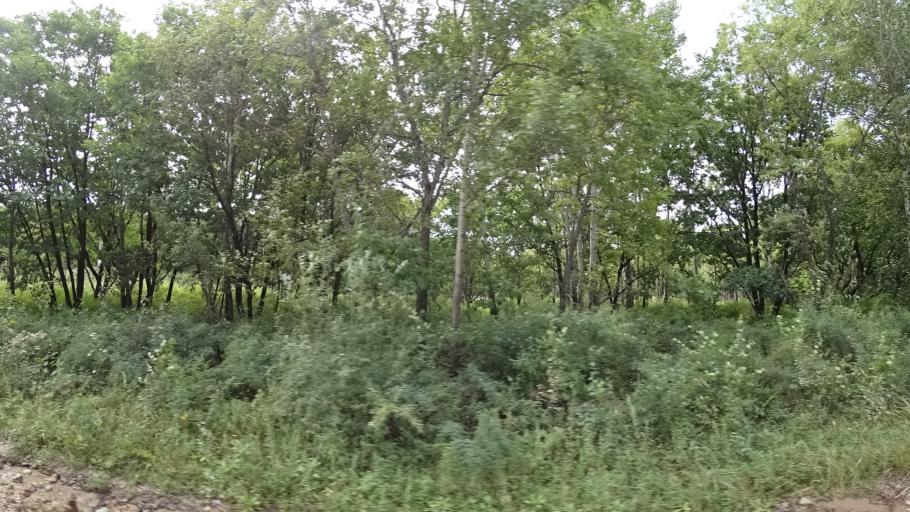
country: RU
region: Primorskiy
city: Lyalichi
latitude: 44.0903
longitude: 132.4344
